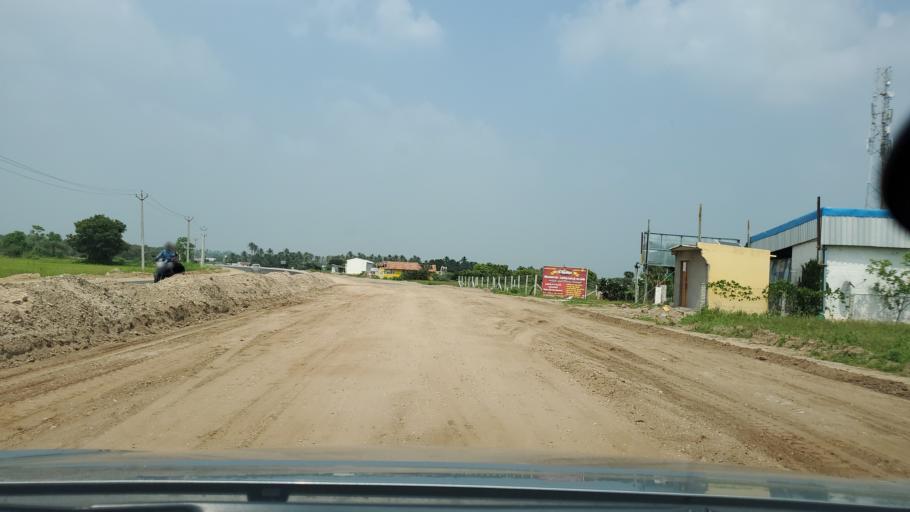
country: IN
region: Tamil Nadu
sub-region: Tiruppur
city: Kangayam
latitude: 10.9193
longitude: 77.4510
